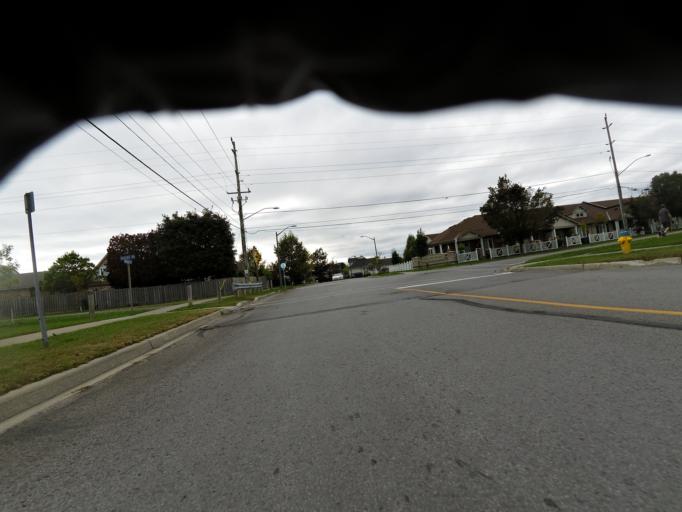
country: CA
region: Ontario
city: Cobourg
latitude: 43.9677
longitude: -78.2012
